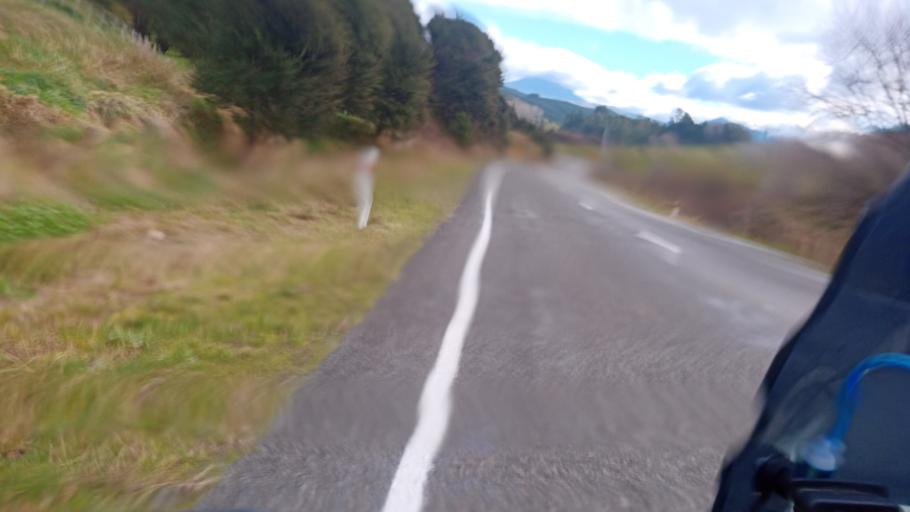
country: NZ
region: Gisborne
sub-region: Gisborne District
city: Gisborne
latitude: -38.0300
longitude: 178.2812
